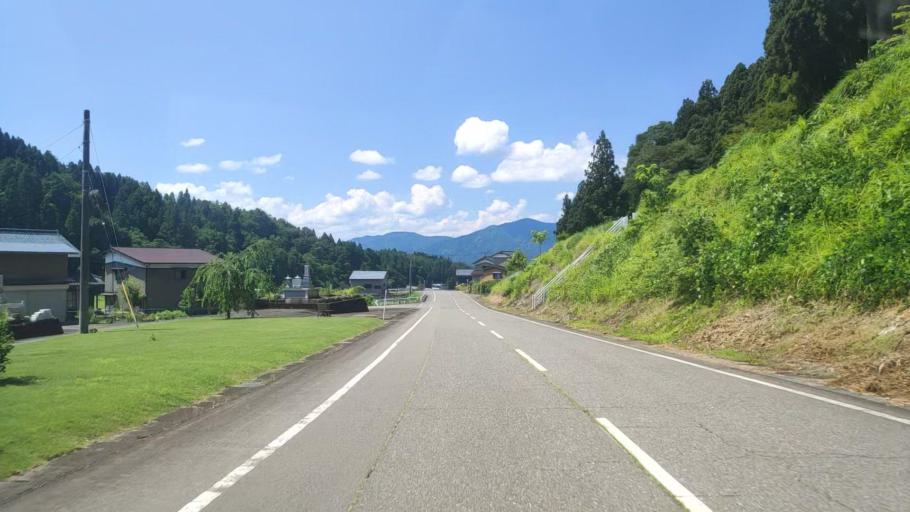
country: JP
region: Fukui
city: Katsuyama
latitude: 36.1058
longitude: 136.4955
